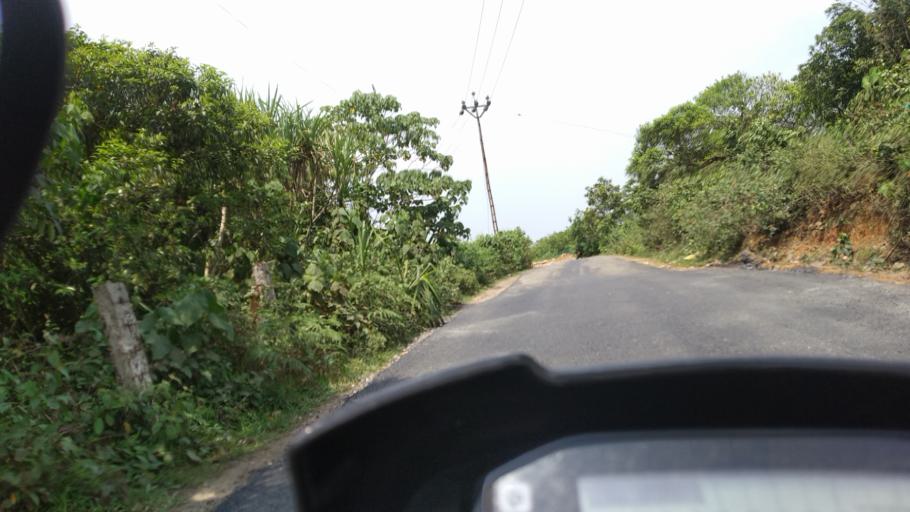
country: IN
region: Kerala
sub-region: Kottayam
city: Erattupetta
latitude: 9.6443
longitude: 76.9268
